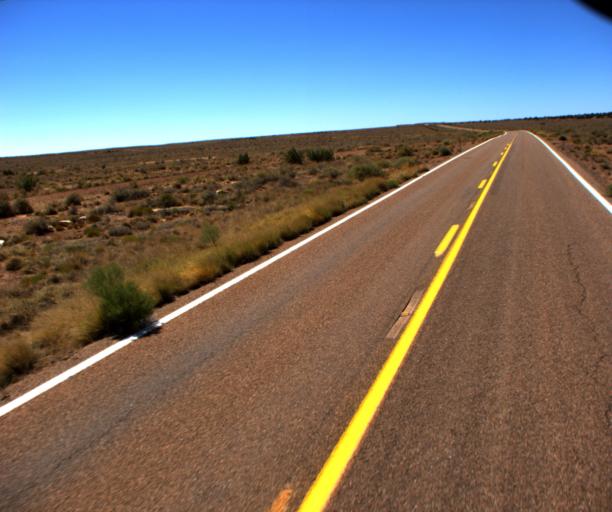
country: US
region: Arizona
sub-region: Navajo County
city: Winslow
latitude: 34.9449
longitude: -110.6450
